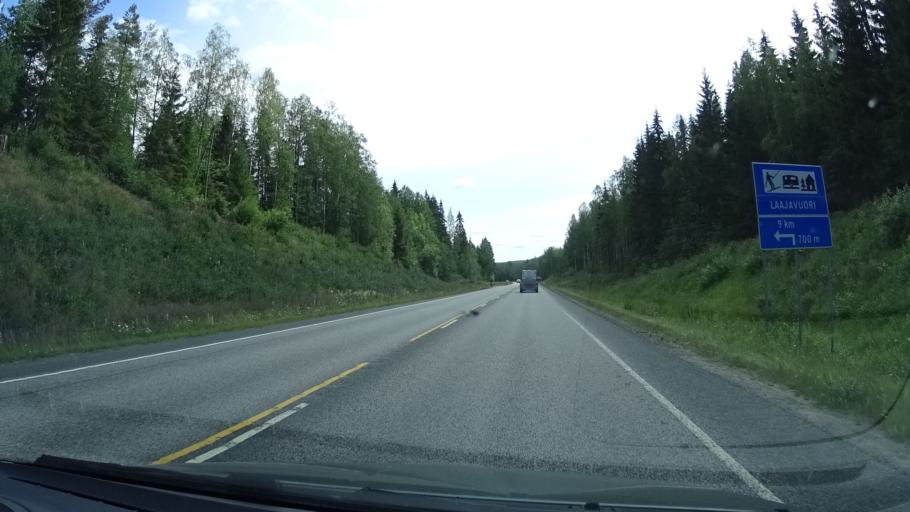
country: FI
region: Central Finland
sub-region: Jyvaeskylae
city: Jyvaeskylae
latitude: 62.2633
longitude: 25.5871
